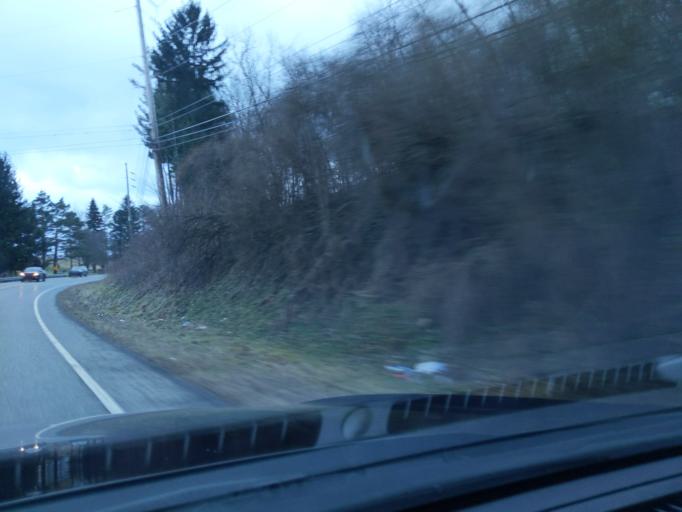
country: US
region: Pennsylvania
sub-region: Blair County
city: Bellwood
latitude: 40.5924
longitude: -78.3362
